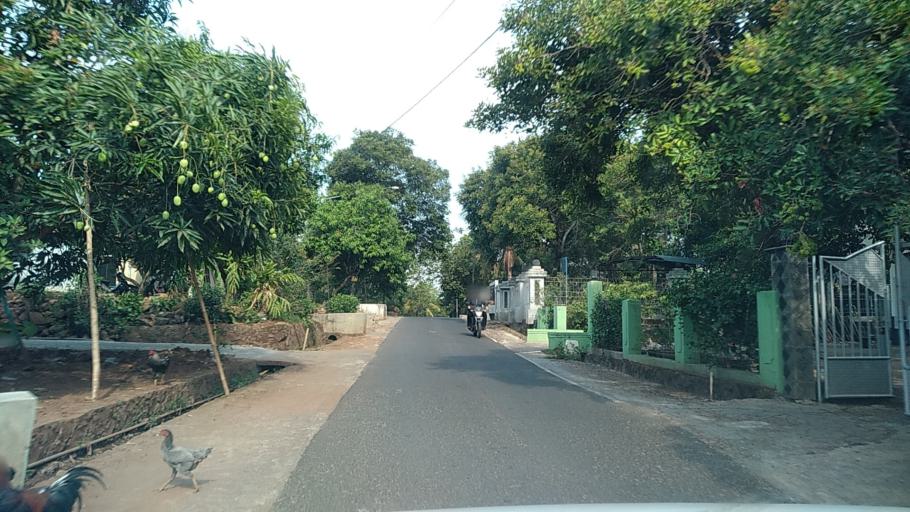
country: ID
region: Central Java
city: Semarang
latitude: -7.0392
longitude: 110.2996
